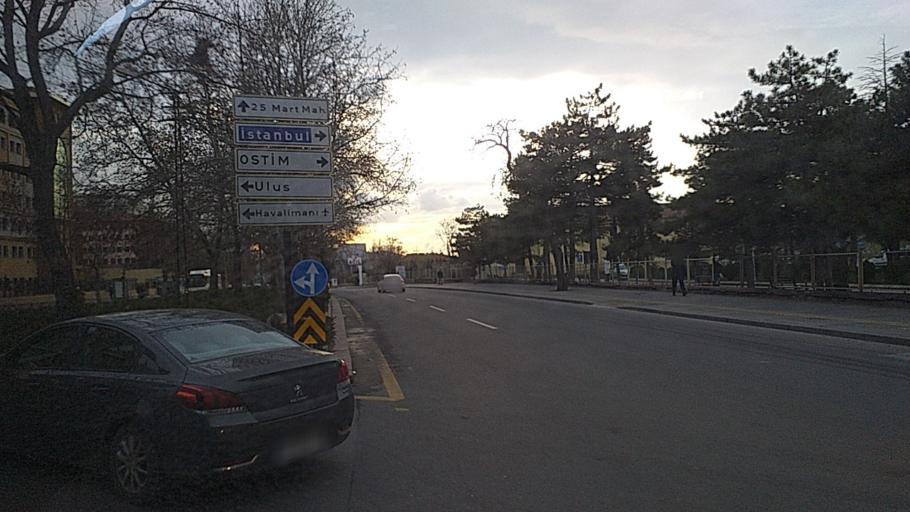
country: TR
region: Ankara
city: Ankara
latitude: 39.9443
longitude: 32.8247
